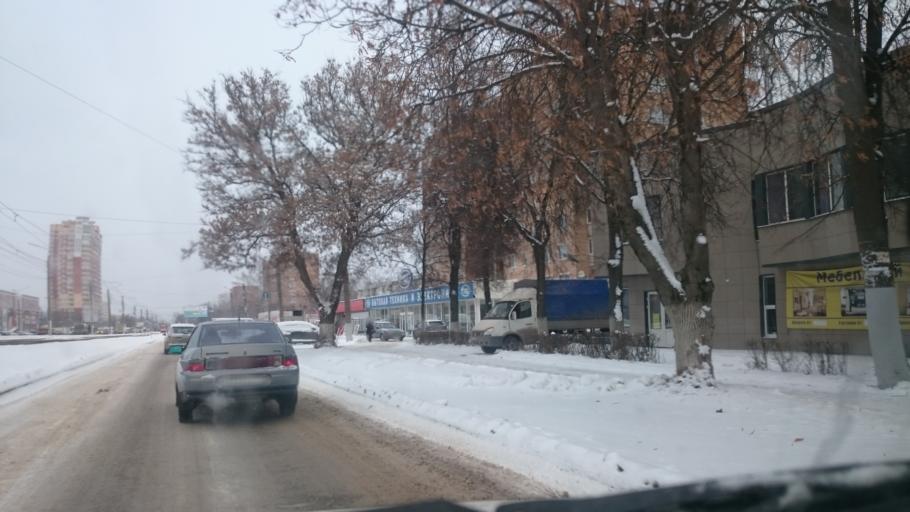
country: RU
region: Tula
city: Mendeleyevskiy
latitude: 54.1504
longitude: 37.5838
